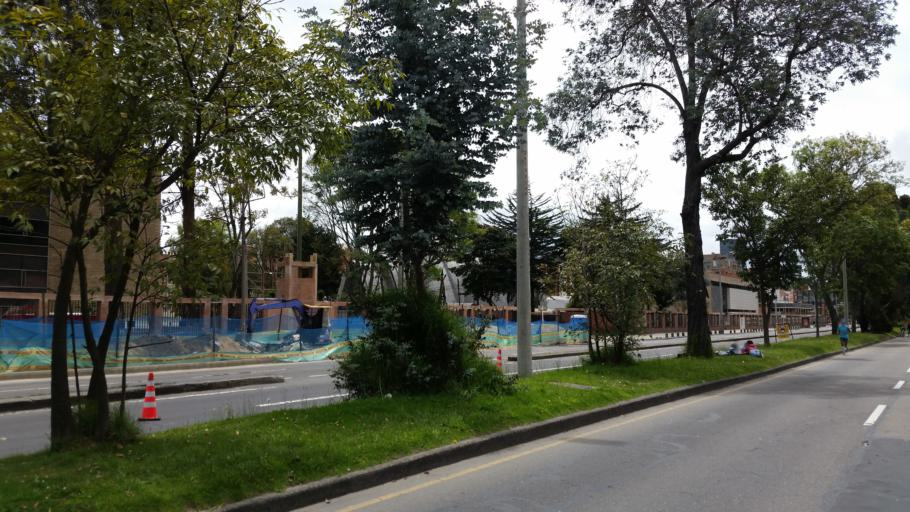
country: CO
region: Bogota D.C.
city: Barrio San Luis
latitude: 4.6826
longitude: -74.0367
